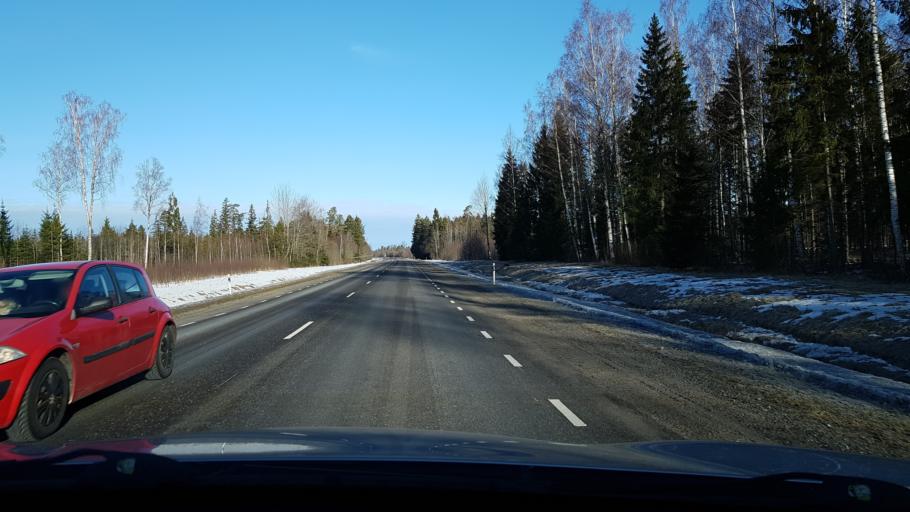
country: EE
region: Viljandimaa
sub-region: Vohma linn
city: Vohma
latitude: 58.6077
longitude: 25.5722
